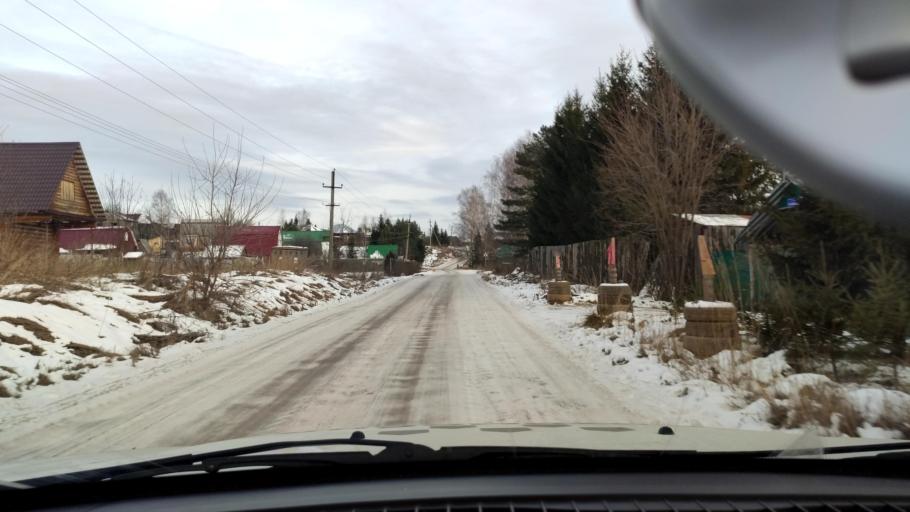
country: RU
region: Perm
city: Lobanovo
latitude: 57.8299
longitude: 56.3584
